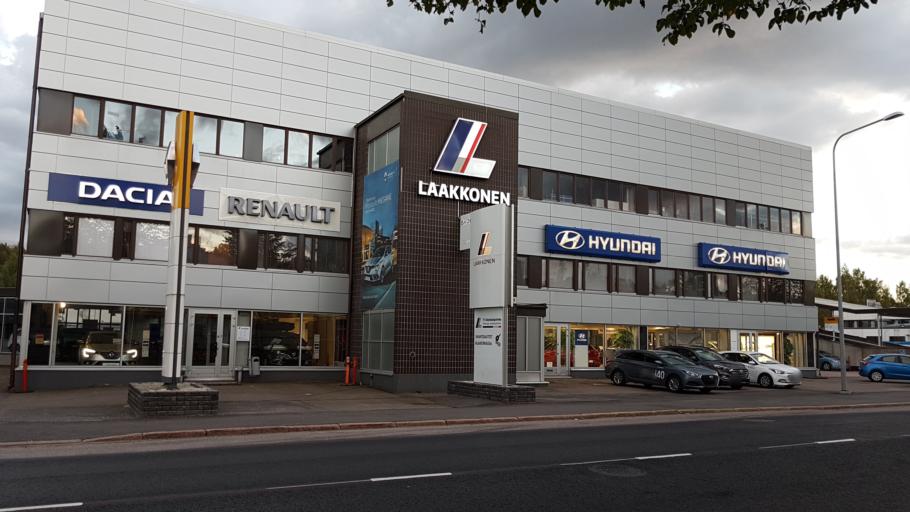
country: FI
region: Uusimaa
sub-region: Helsinki
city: Vantaa
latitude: 60.2028
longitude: 25.0456
